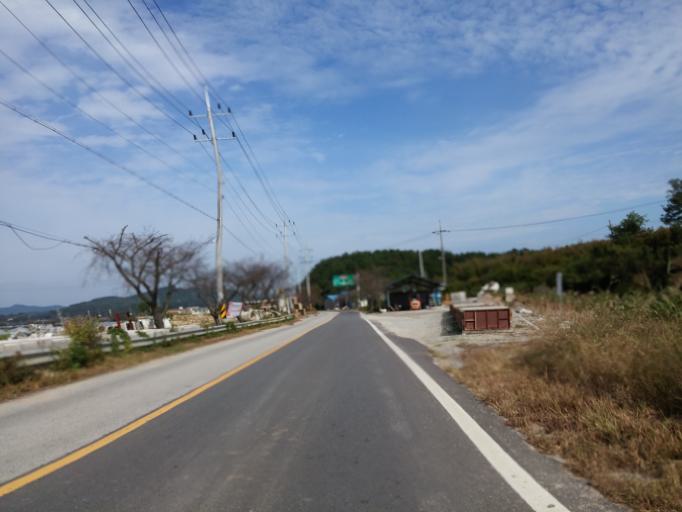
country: KR
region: Chungcheongnam-do
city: Nonsan
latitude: 36.1745
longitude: 127.1244
